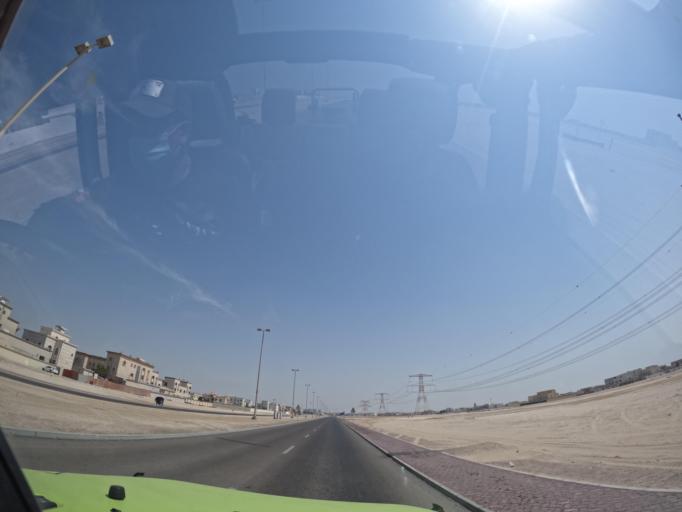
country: AE
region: Abu Dhabi
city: Abu Dhabi
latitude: 24.3065
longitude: 54.5689
